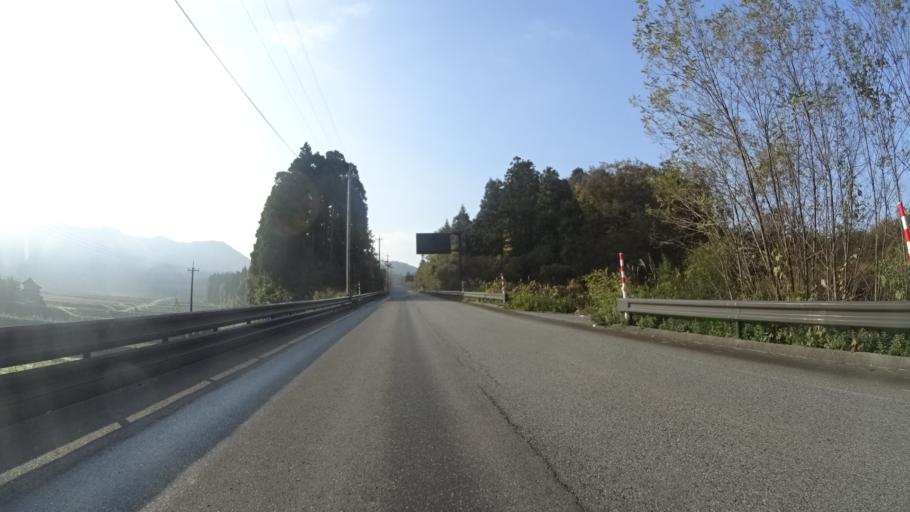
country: JP
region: Ishikawa
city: Nanao
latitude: 37.0266
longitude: 136.9855
